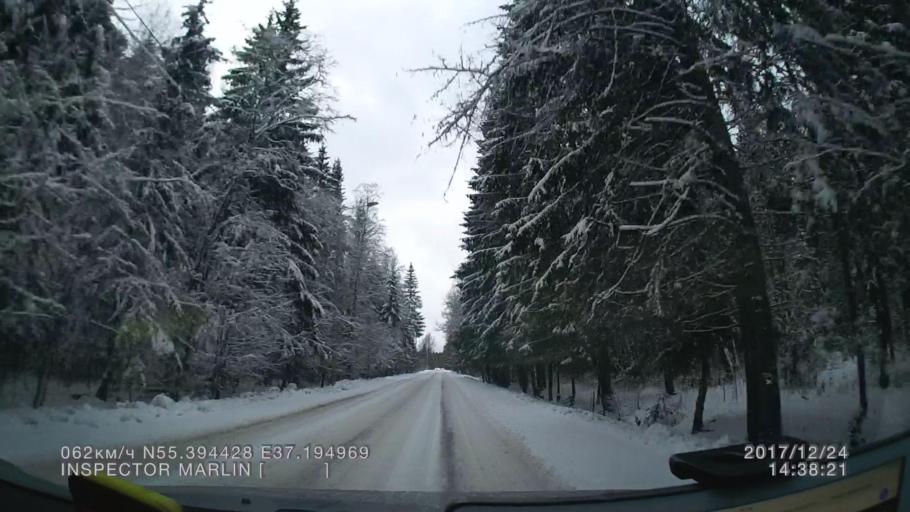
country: RU
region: Moskovskaya
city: Troitsk
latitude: 55.3942
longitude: 37.1951
